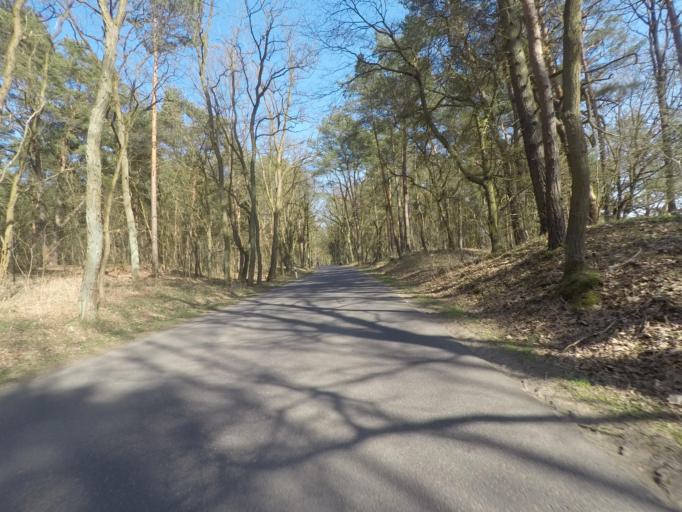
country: DE
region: Brandenburg
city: Melchow
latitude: 52.8623
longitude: 13.6976
